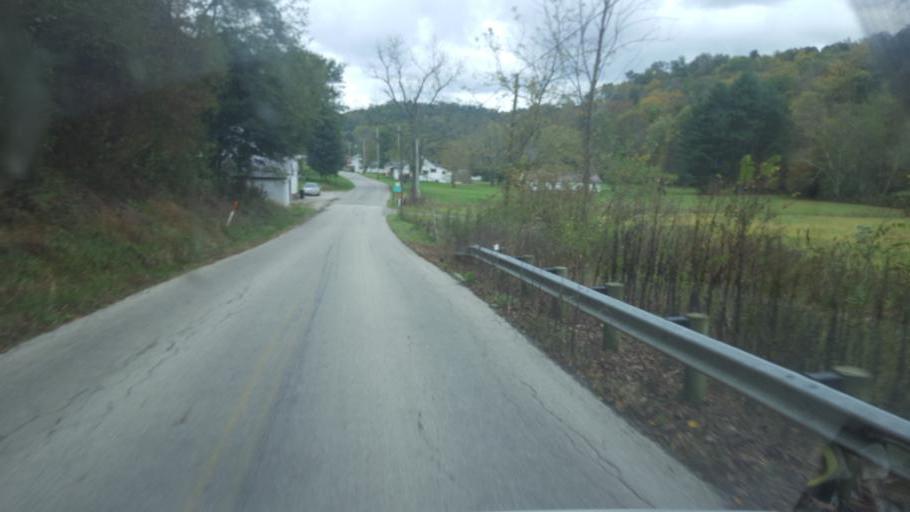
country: US
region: Ohio
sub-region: Ashland County
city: Loudonville
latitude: 40.5254
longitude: -82.1024
